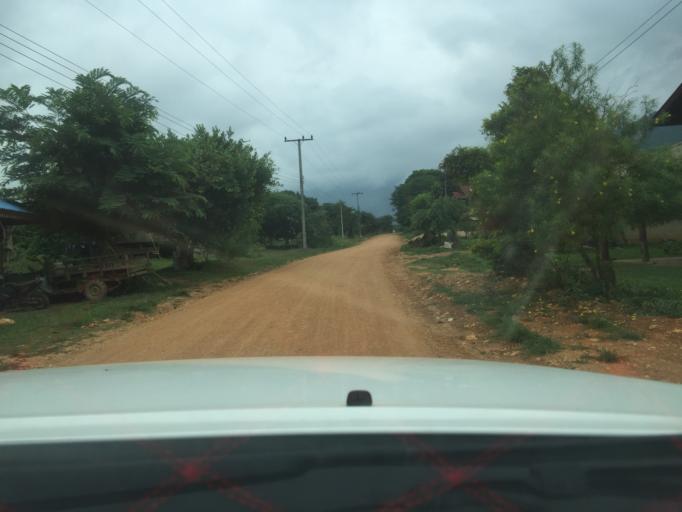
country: TH
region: Phayao
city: Phu Sang
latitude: 19.7381
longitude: 100.4676
